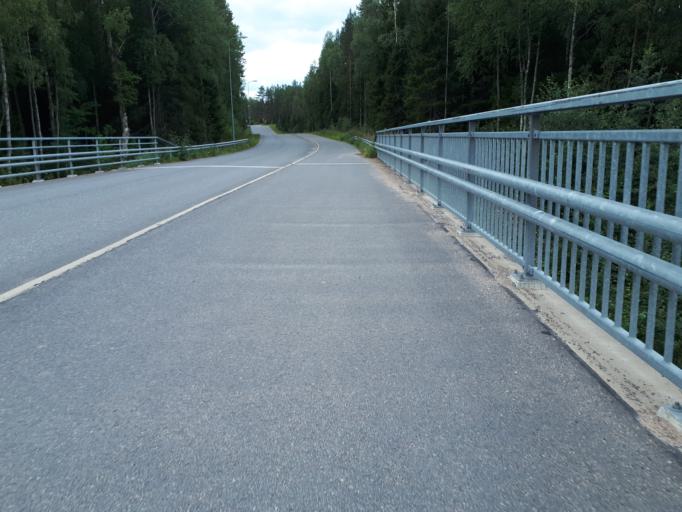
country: FI
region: Northern Ostrobothnia
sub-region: Oulunkaari
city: Ii
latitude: 65.3220
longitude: 25.4100
